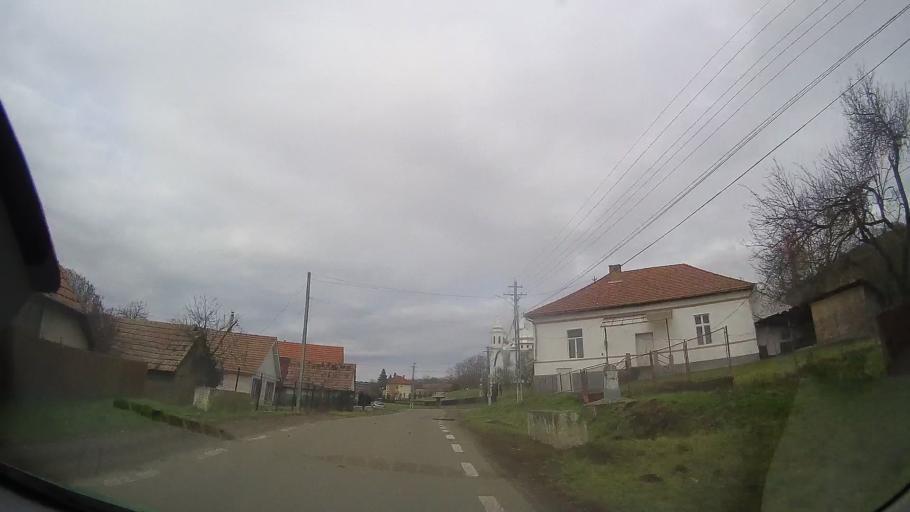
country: RO
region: Mures
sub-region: Comuna Cozma
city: Cozma
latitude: 46.8073
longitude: 24.5235
